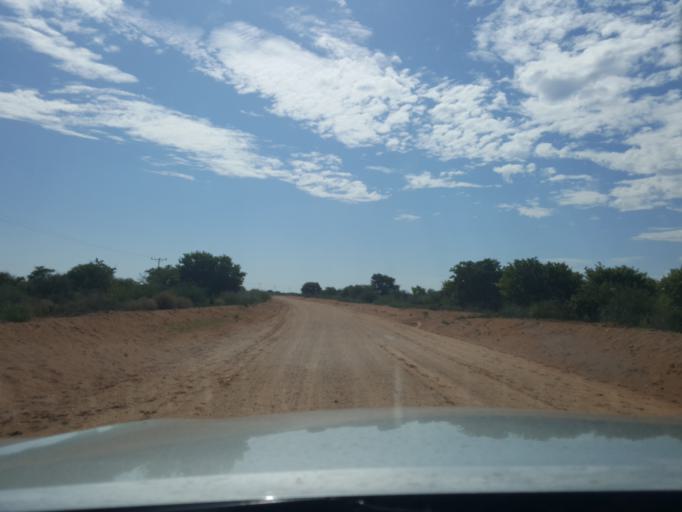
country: BW
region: Kweneng
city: Khudumelapye
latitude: -23.8497
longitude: 24.8698
